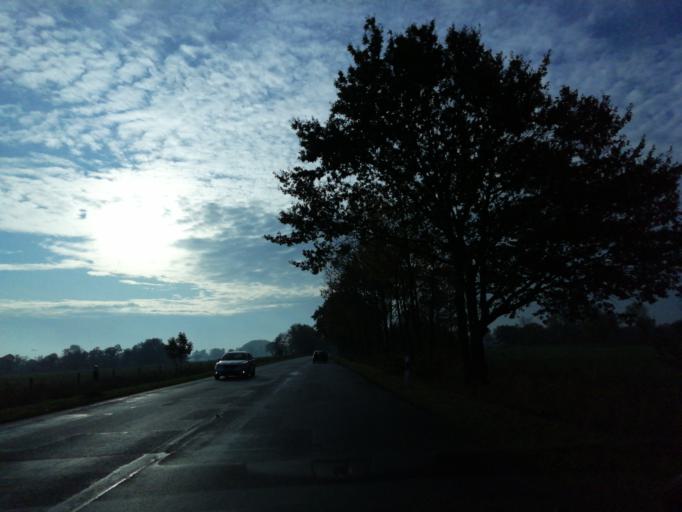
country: DE
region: Lower Saxony
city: Fedderwarden
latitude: 53.6014
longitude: 8.0487
